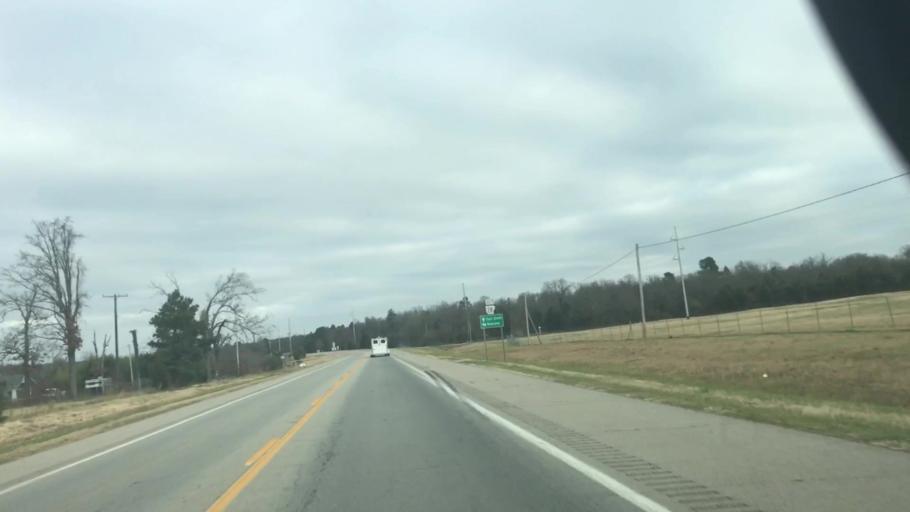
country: US
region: Arkansas
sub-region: Scott County
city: Waldron
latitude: 34.9373
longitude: -94.1022
